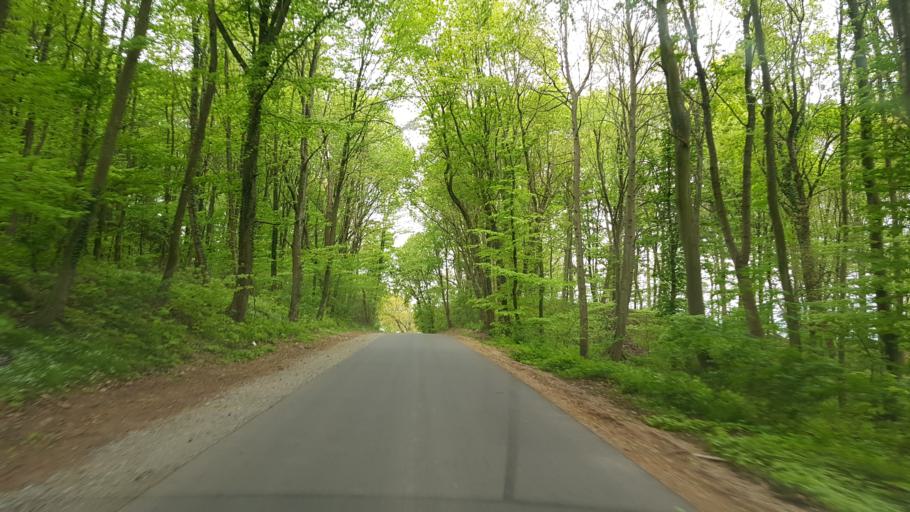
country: PL
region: West Pomeranian Voivodeship
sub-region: Powiat slawienski
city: Slawno
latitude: 54.2694
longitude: 16.5494
